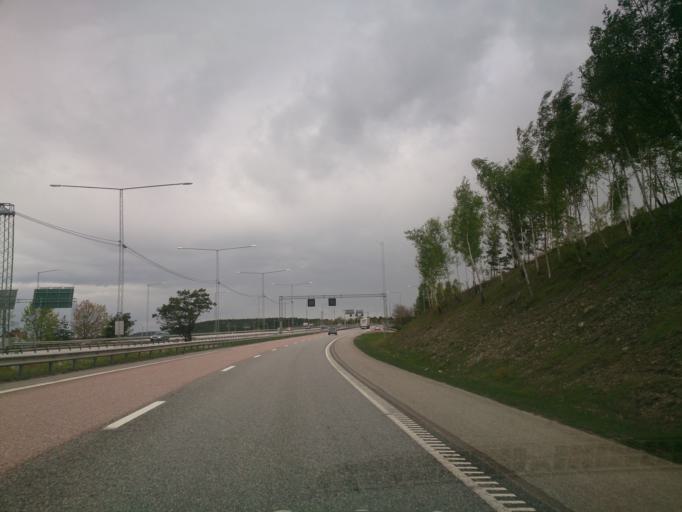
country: SE
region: Stockholm
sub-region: Sodertalje Kommun
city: Soedertaelje
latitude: 59.1794
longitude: 17.6421
